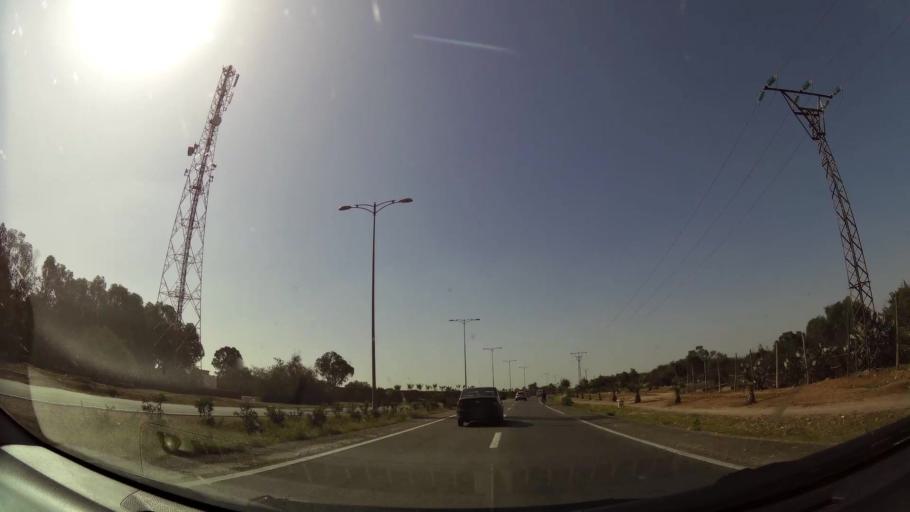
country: MA
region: Souss-Massa-Draa
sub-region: Inezgane-Ait Mellou
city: Inezgane
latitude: 30.3473
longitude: -9.4788
